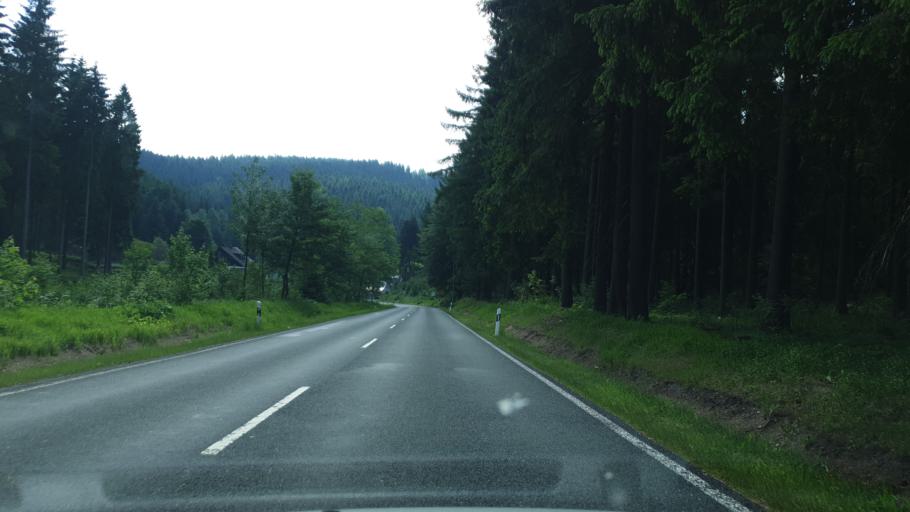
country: DE
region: Saxony
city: Klingenthal
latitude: 50.4000
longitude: 12.4921
